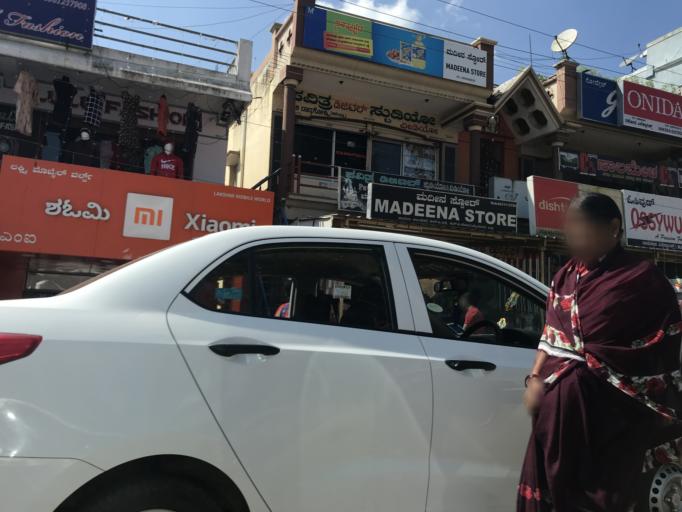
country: IN
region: Karnataka
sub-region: Mysore
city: Heggadadevankote
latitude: 12.0858
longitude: 76.3330
